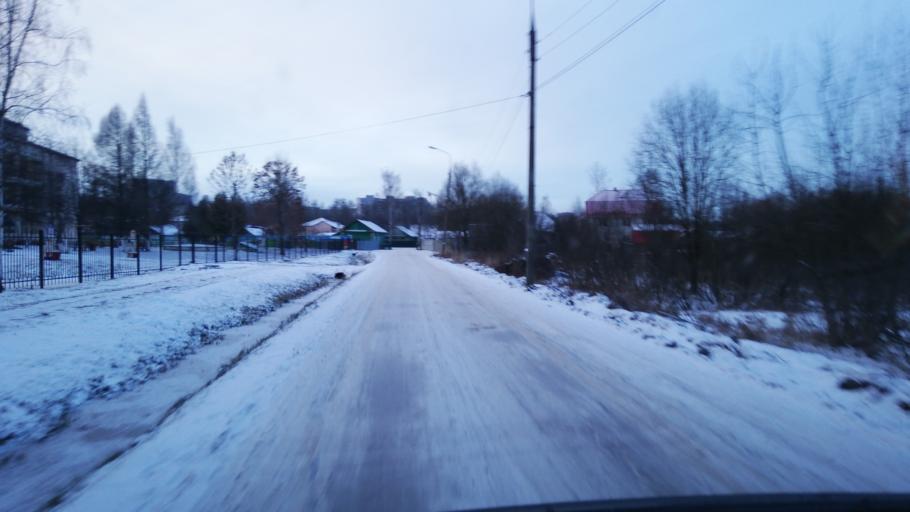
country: RU
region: Jaroslavl
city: Yaroslavl
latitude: 57.5970
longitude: 39.8421
